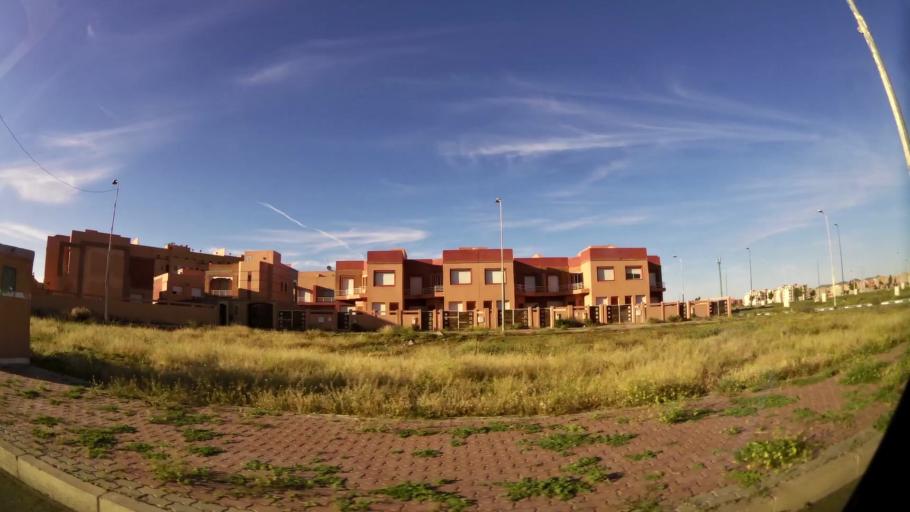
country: MA
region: Marrakech-Tensift-Al Haouz
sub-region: Marrakech
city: Marrakesh
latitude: 31.7621
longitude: -8.1088
